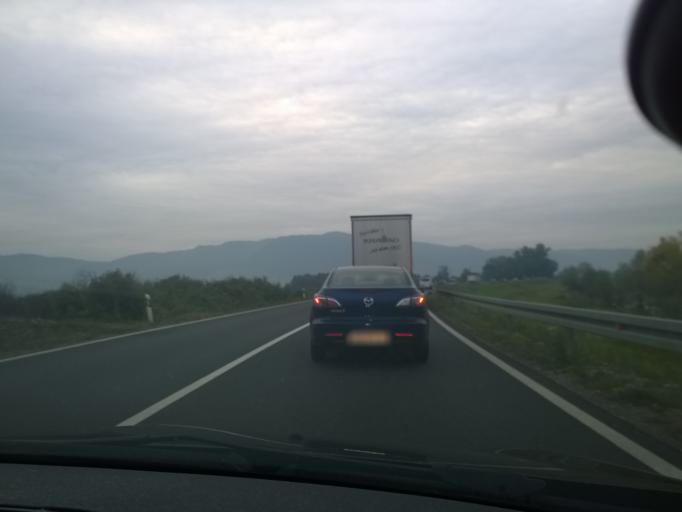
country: HR
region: Zagrebacka
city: Pojatno
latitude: 45.8940
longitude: 15.8201
